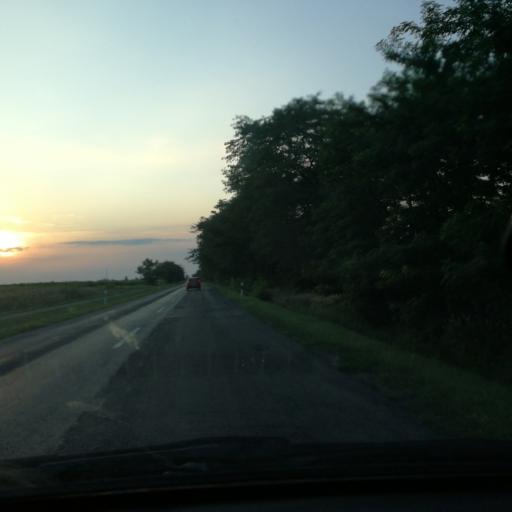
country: HU
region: Bacs-Kiskun
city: Kiskoros
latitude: 46.5954
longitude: 19.3314
